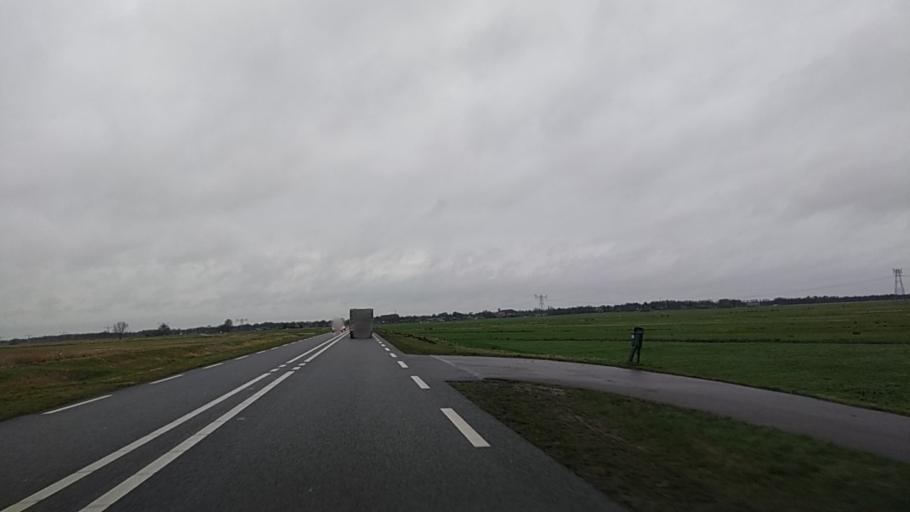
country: NL
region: Overijssel
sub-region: Gemeente Steenwijkerland
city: Sint Jansklooster
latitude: 52.6428
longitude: 6.0237
